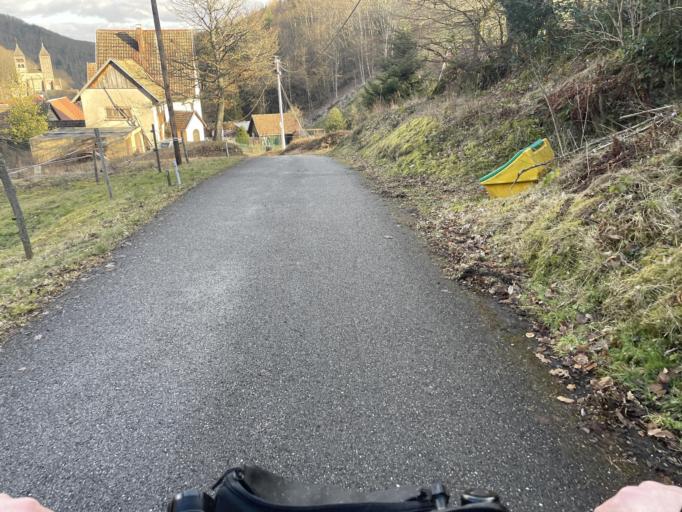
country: FR
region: Alsace
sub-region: Departement du Haut-Rhin
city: Lautenbach
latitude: 47.9226
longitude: 7.1520
